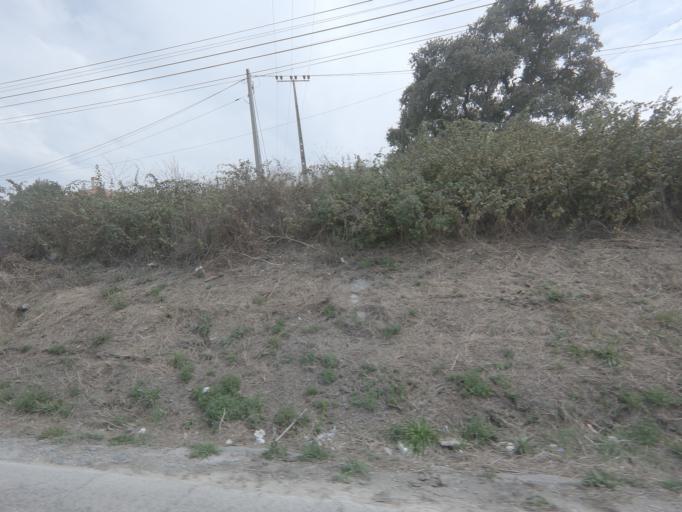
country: PT
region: Leiria
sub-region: Leiria
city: Caranguejeira
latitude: 39.8123
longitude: -8.7373
